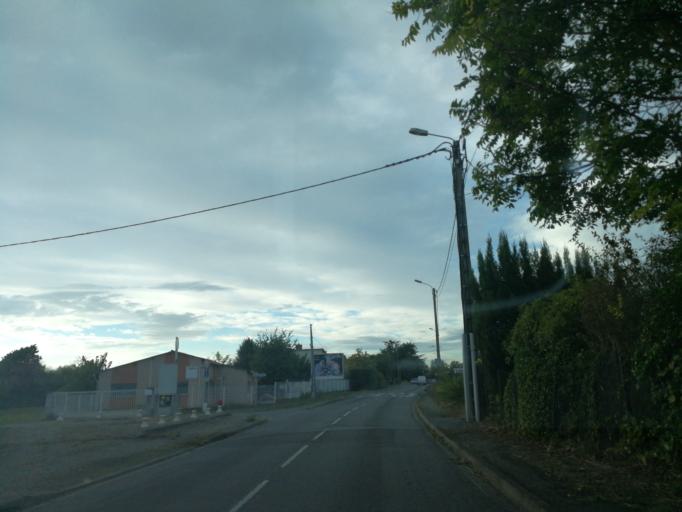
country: FR
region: Midi-Pyrenees
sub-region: Departement de la Haute-Garonne
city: L'Union
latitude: 43.6619
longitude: 1.4655
